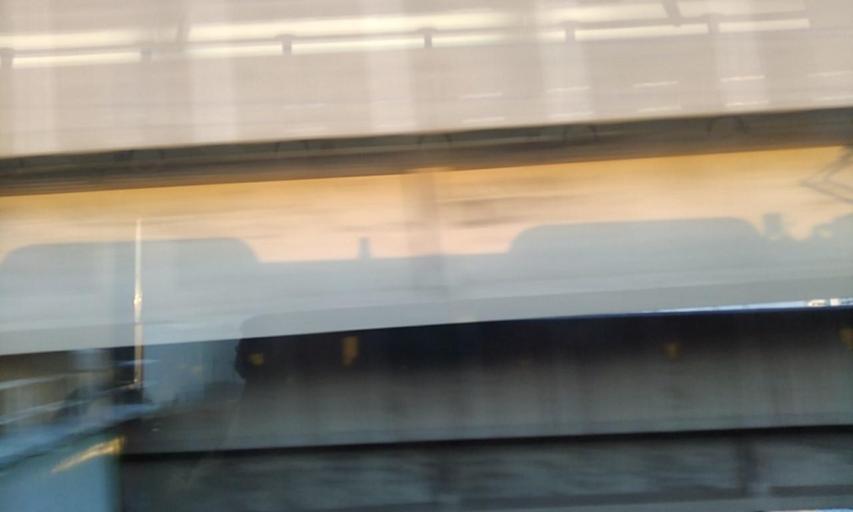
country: JP
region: Kagawa
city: Sakaidecho
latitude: 34.3203
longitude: 133.8228
